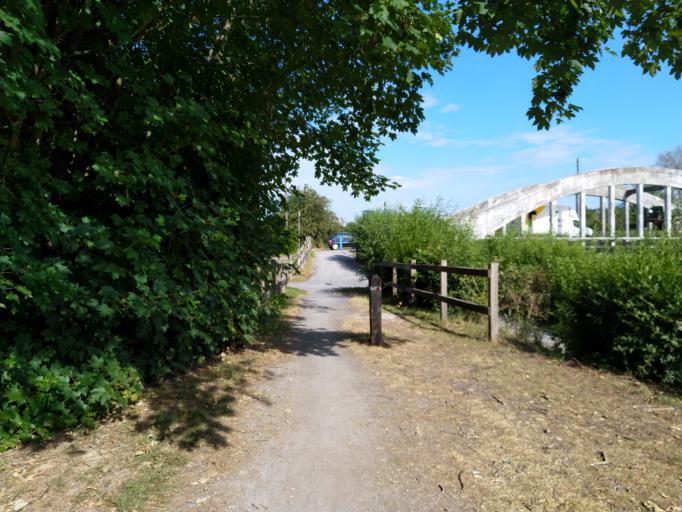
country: FR
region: Nord-Pas-de-Calais
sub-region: Departement du Nord
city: Rousies
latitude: 50.2835
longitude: 4.0154
